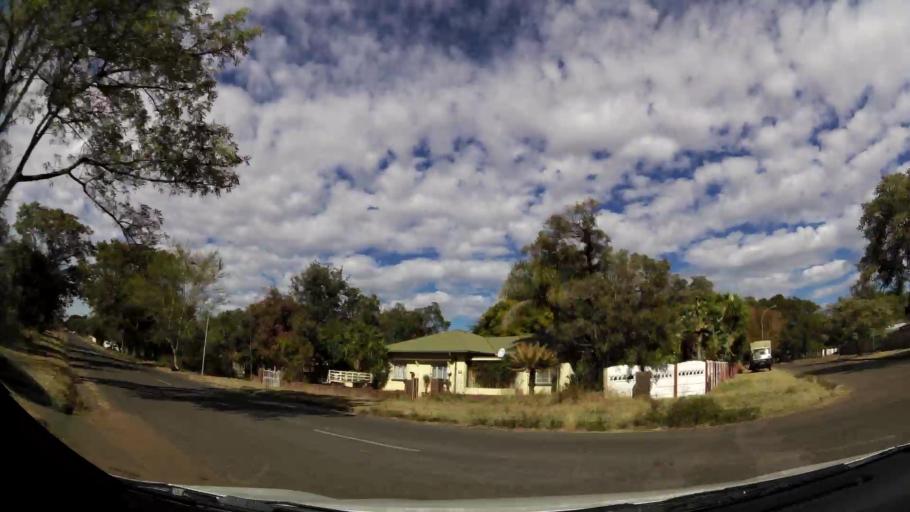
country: ZA
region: Limpopo
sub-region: Waterberg District Municipality
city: Bela-Bela
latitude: -24.8773
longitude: 28.2927
